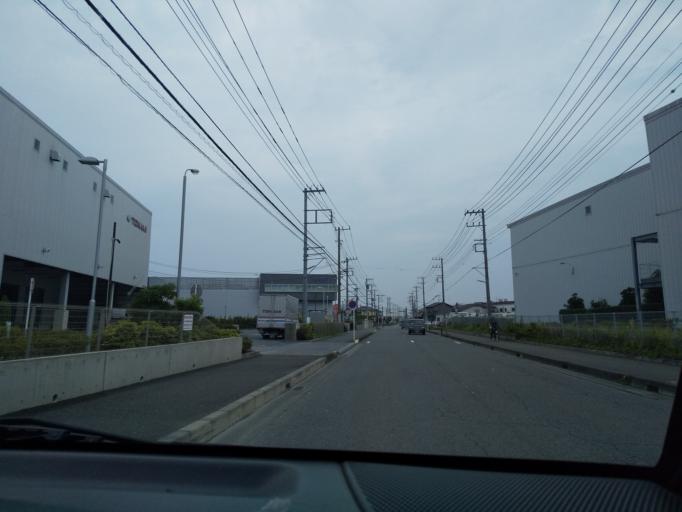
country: JP
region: Kanagawa
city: Atsugi
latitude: 35.4053
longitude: 139.3877
